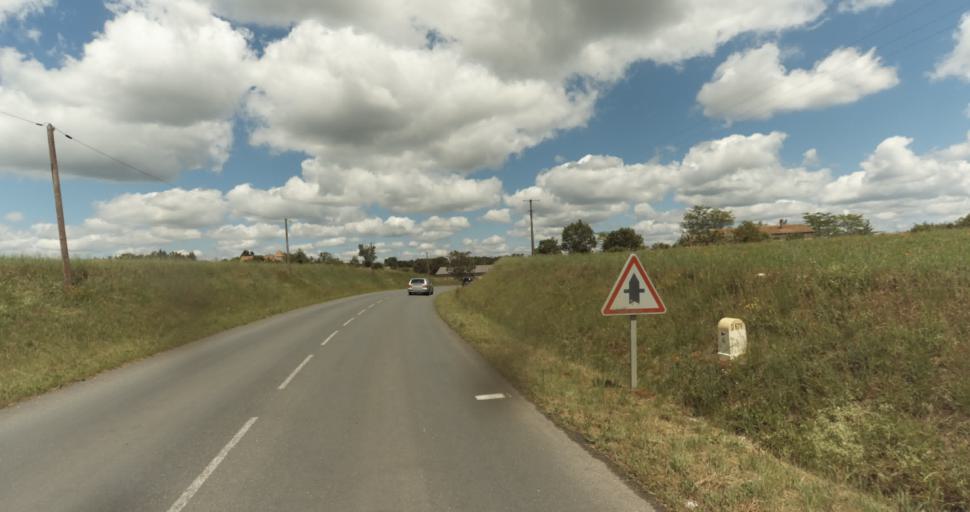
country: FR
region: Aquitaine
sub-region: Departement de la Dordogne
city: Beaumont-du-Perigord
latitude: 44.7385
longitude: 0.7516
